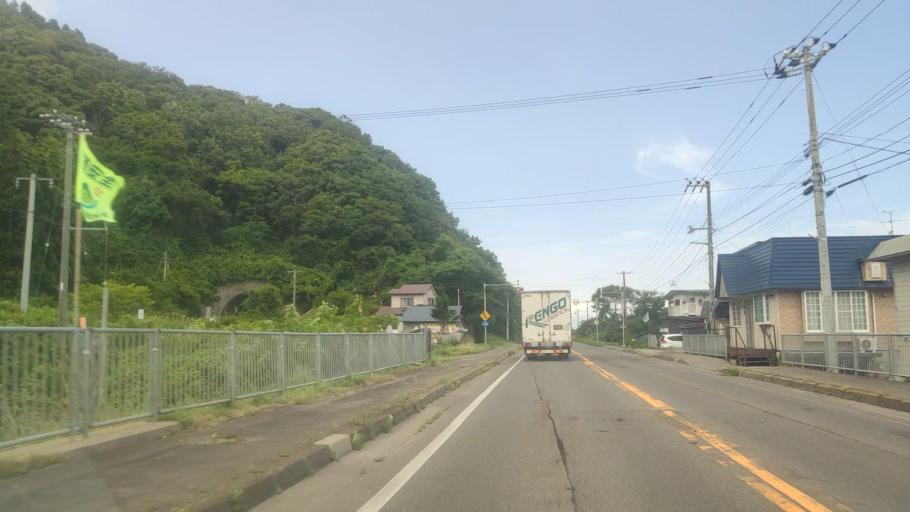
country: JP
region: Hokkaido
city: Nanae
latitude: 42.1612
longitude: 140.4707
